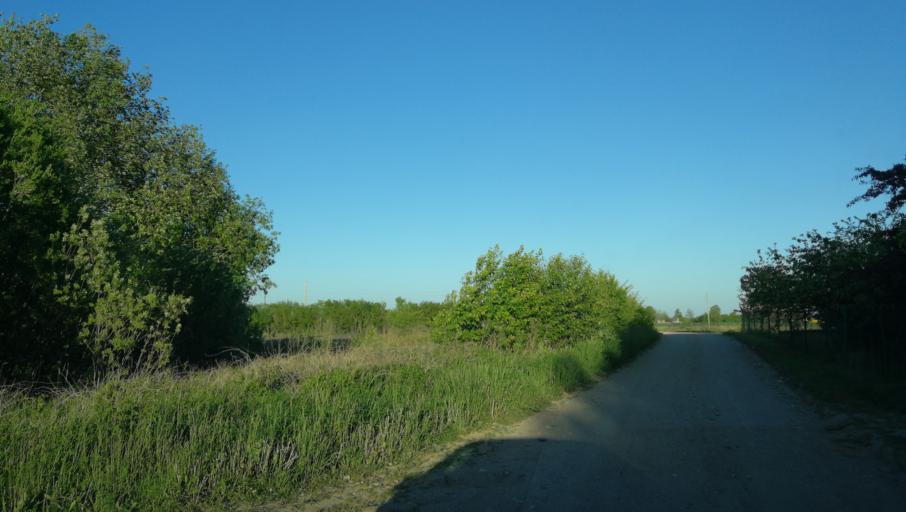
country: LV
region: Dobeles Rajons
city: Dobele
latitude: 56.6190
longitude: 23.3002
